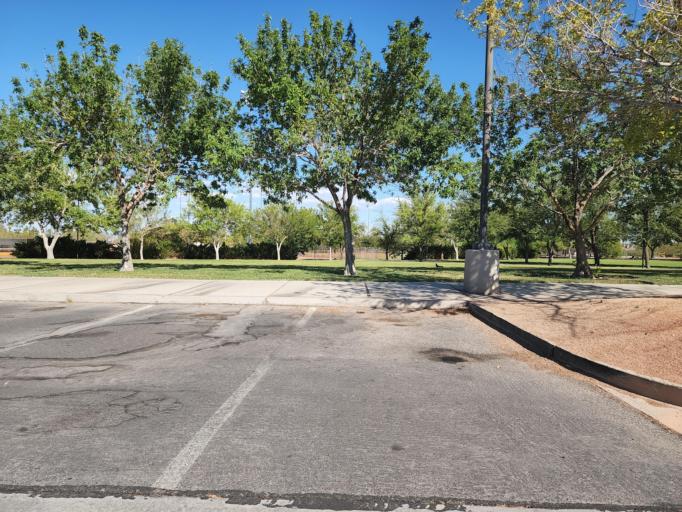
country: US
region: Nevada
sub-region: Clark County
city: Spring Valley
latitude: 36.1491
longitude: -115.2493
